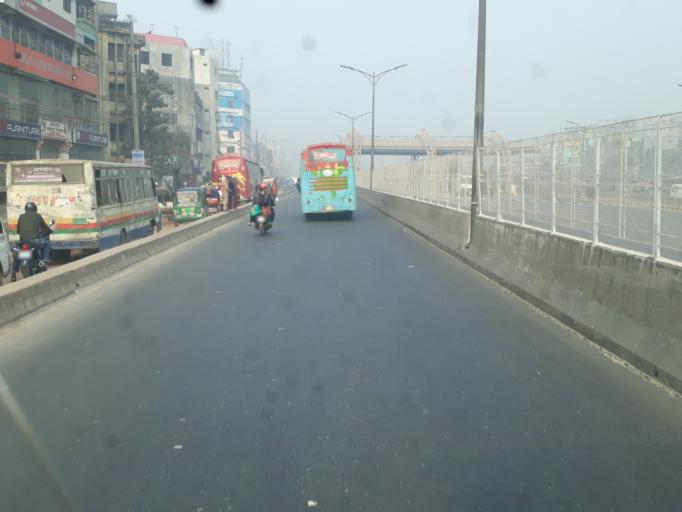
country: BD
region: Dhaka
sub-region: Dhaka
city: Dhaka
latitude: 23.7063
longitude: 90.4422
